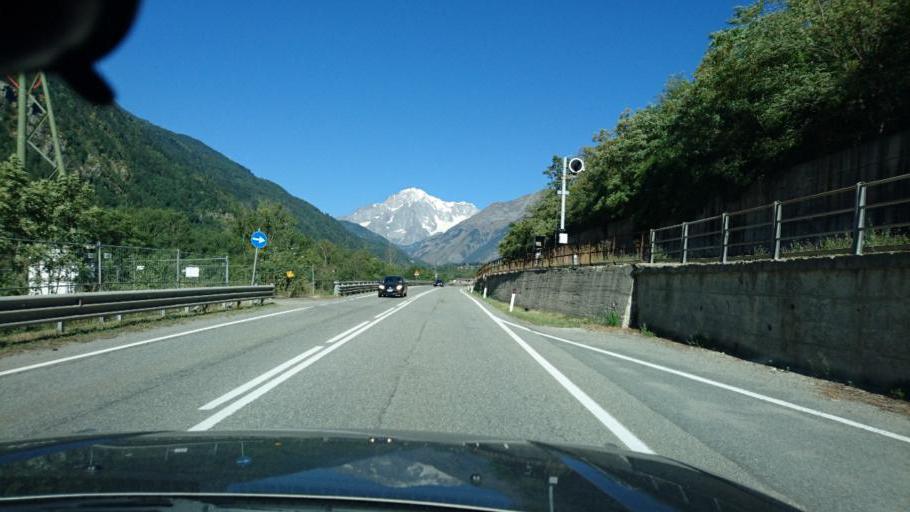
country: IT
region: Aosta Valley
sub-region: Valle d'Aosta
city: Avise
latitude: 45.7198
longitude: 7.1042
